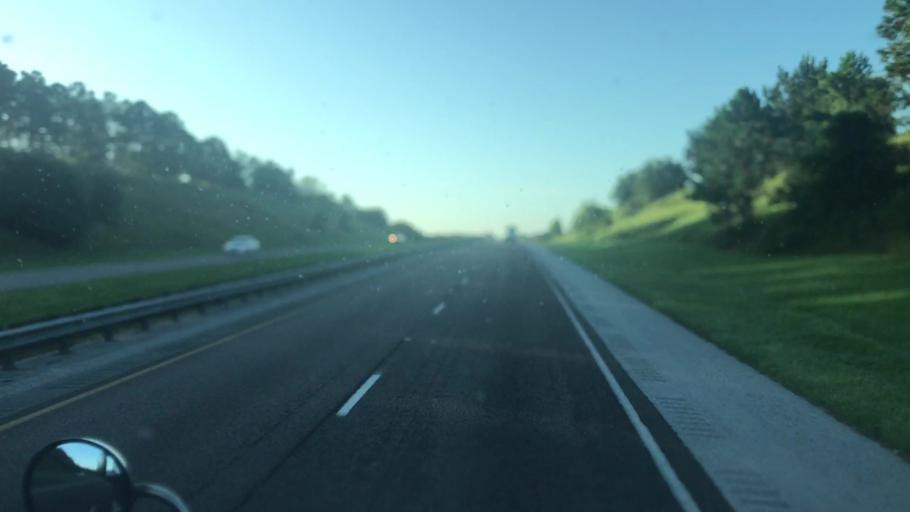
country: US
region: Florida
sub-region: Lake County
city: Montverde
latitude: 28.5722
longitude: -81.6965
